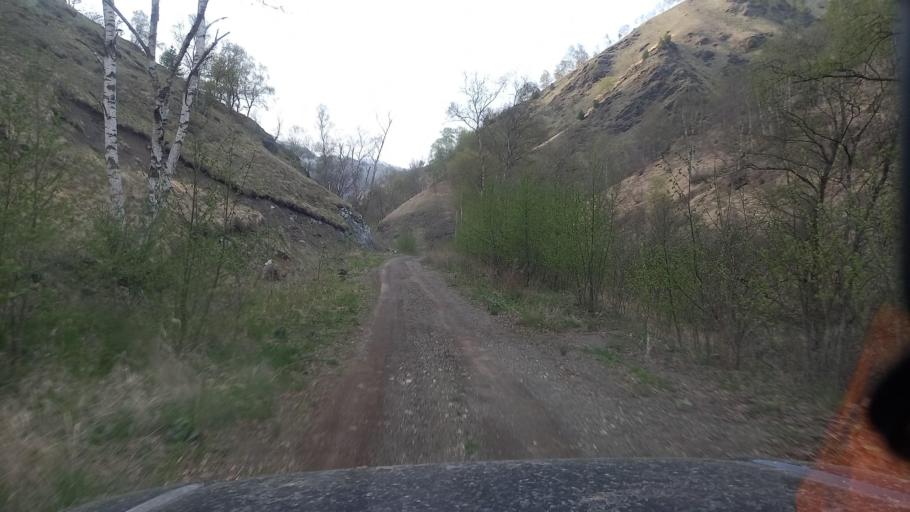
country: RU
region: Kabardino-Balkariya
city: Kamennomostskoye
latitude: 43.7094
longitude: 42.8468
